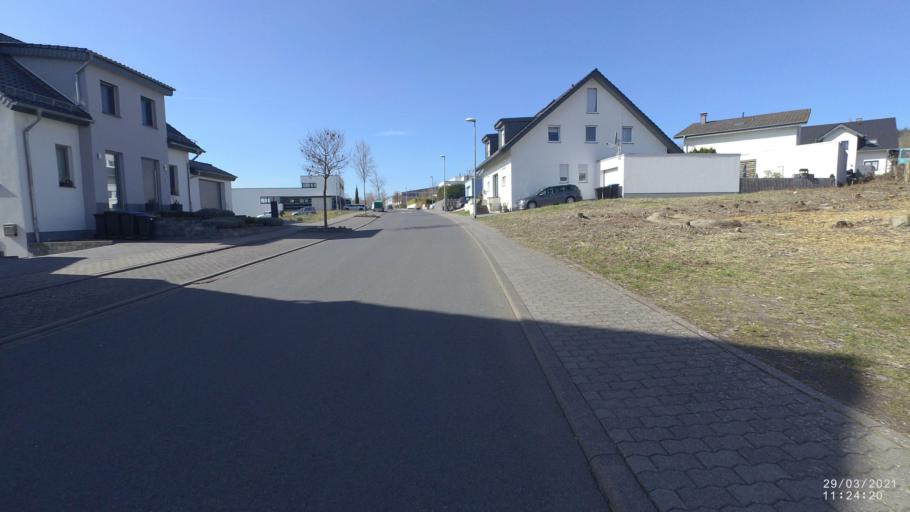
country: DE
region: Rheinland-Pfalz
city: Nickenich
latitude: 50.4241
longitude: 7.3484
